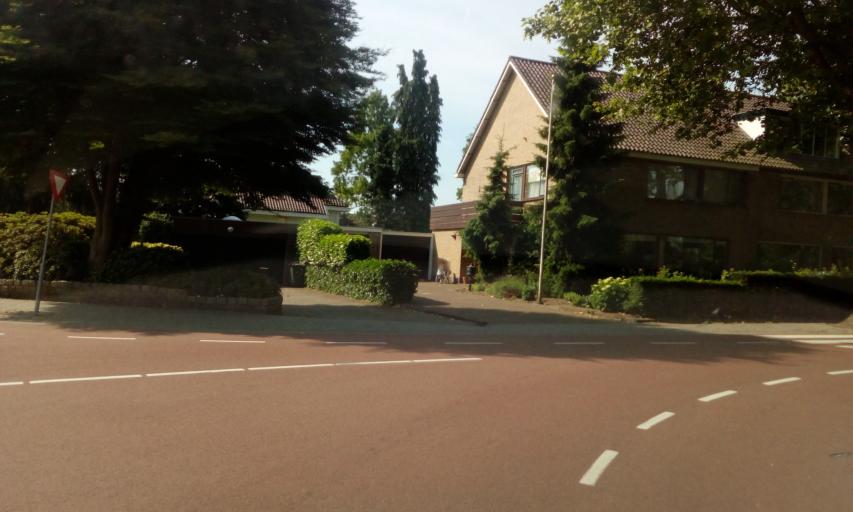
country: NL
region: Utrecht
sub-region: Stichtse Vecht
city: Maarssen
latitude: 52.1387
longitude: 5.0437
